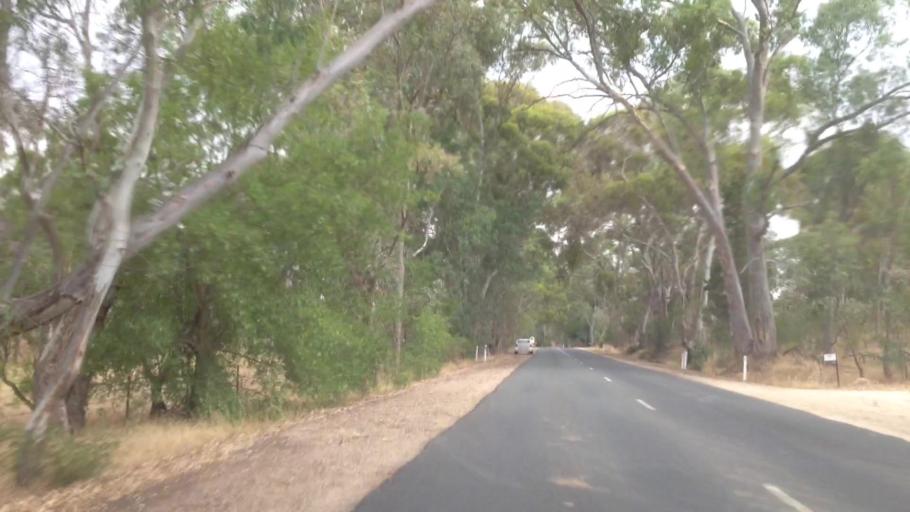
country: AU
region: South Australia
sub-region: Barossa
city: Williamstown
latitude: -34.6648
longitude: 138.8717
